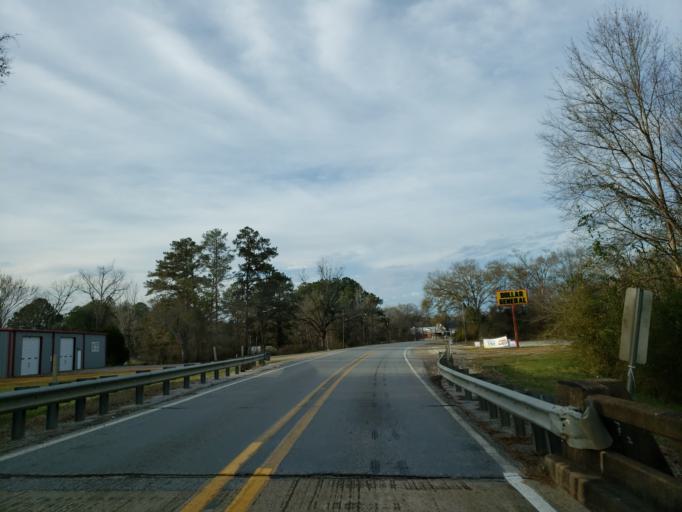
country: US
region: Mississippi
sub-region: Clarke County
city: Quitman
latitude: 31.8562
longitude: -88.6978
